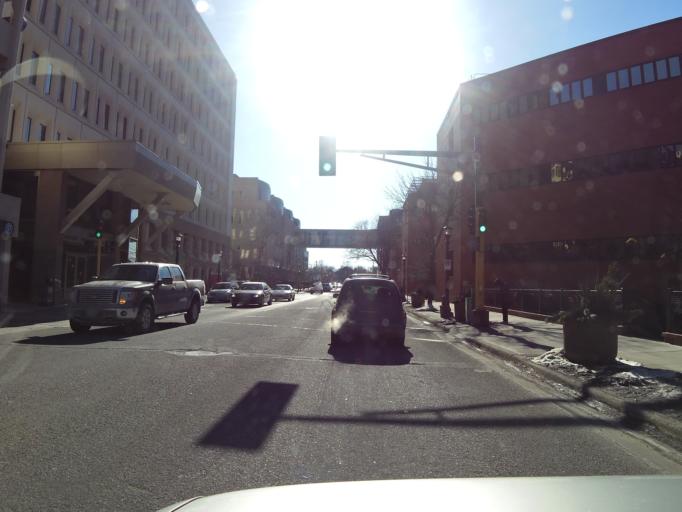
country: US
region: Minnesota
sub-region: Ramsey County
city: Saint Paul
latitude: 44.9430
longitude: -93.1070
